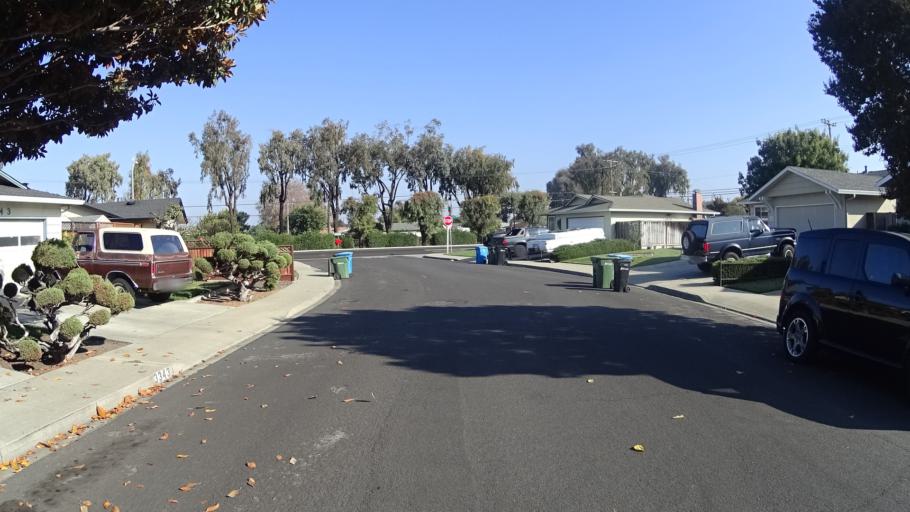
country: US
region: California
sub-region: Santa Clara County
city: Santa Clara
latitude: 37.3626
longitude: -121.9874
